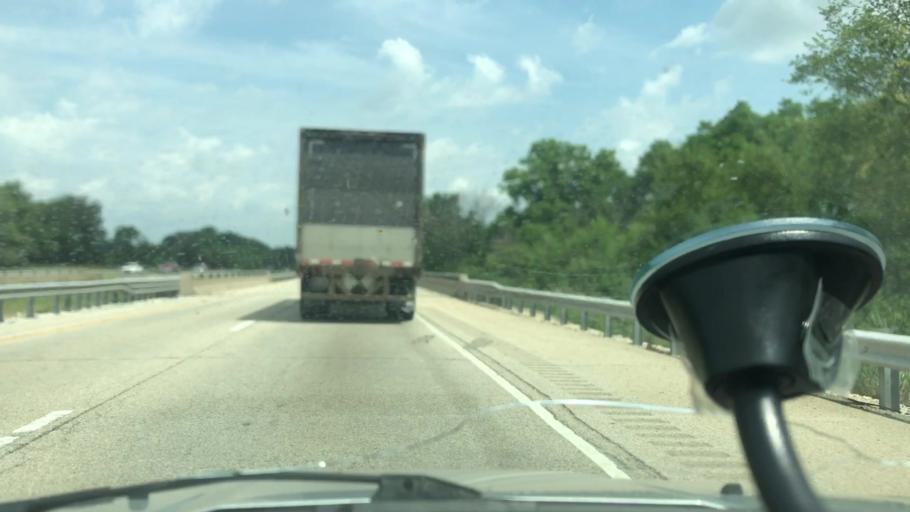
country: US
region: Illinois
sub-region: Peoria County
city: Bellevue
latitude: 40.7177
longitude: -89.6762
